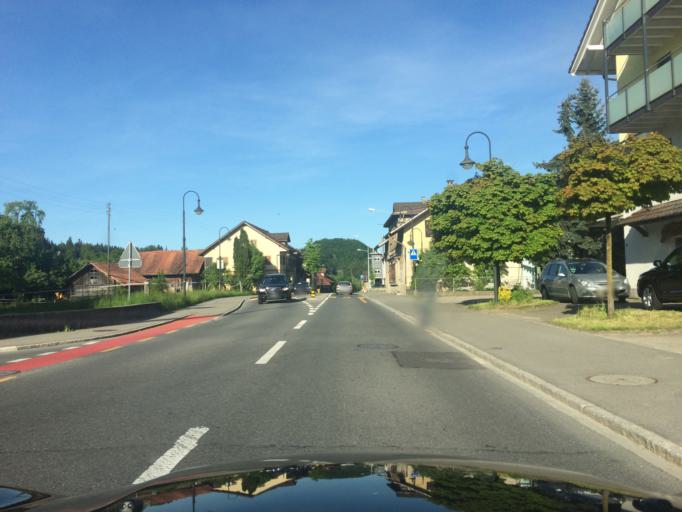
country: CH
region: Lucerne
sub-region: Willisau District
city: Willisau
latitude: 47.1413
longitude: 7.9725
